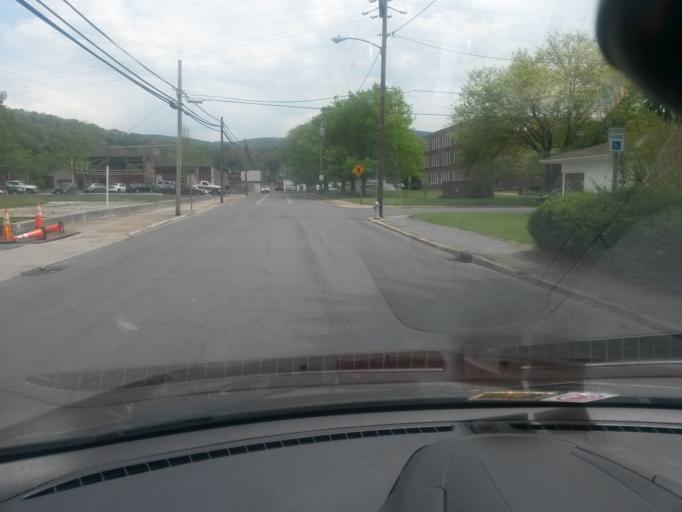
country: US
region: Virginia
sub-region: City of Covington
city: Covington
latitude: 37.7852
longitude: -79.9922
